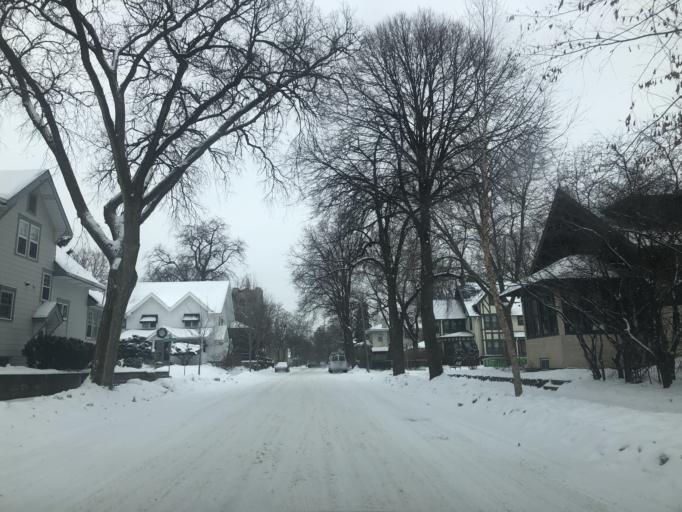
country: US
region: Minnesota
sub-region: Hennepin County
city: Richfield
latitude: 44.9286
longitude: -93.2864
